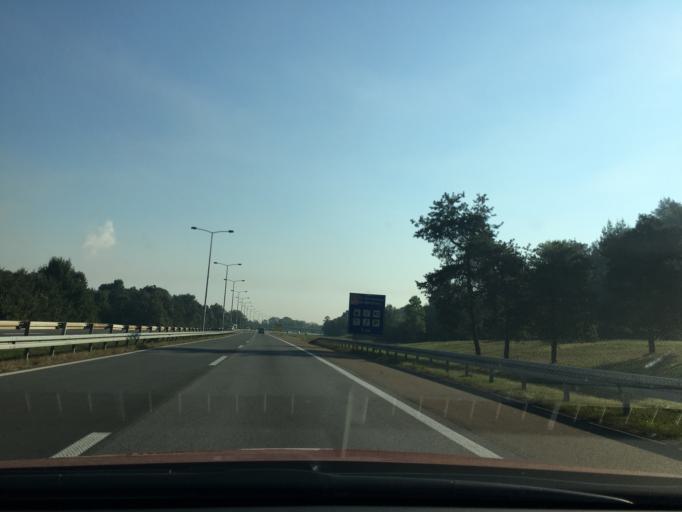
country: RS
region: Central Serbia
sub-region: Podunavski Okrug
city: Smederevo
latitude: 44.5815
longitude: 20.9524
